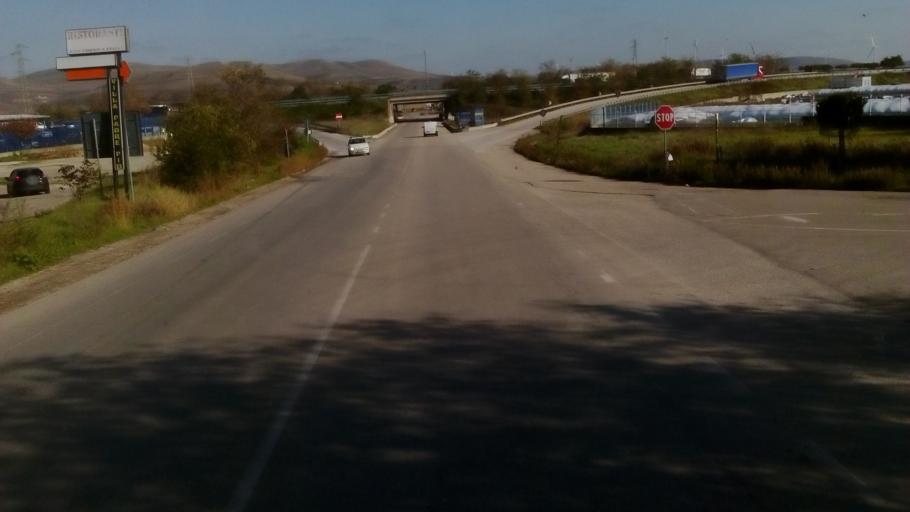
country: IT
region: Apulia
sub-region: Provincia di Foggia
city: Candela
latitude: 41.1504
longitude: 15.5280
